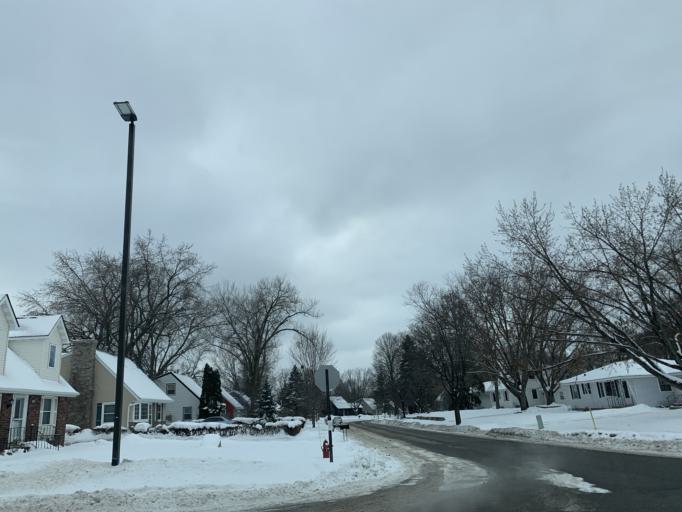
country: US
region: Minnesota
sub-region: Anoka County
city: Blaine
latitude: 45.1675
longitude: -93.2766
